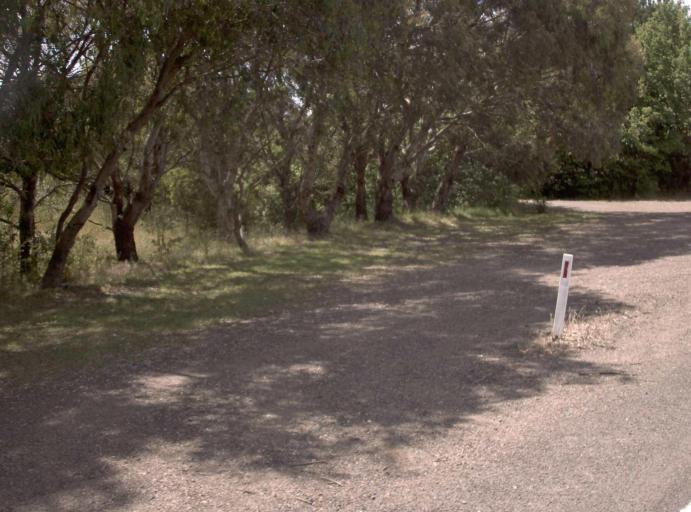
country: AU
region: Victoria
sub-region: Wellington
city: Sale
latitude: -37.9900
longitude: 147.0661
